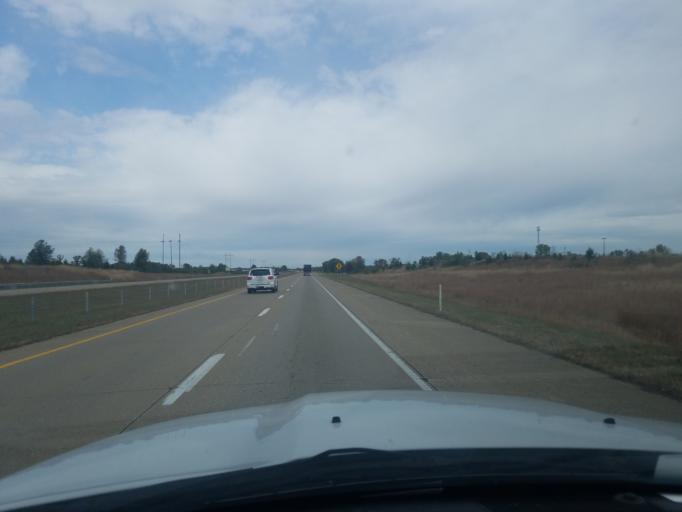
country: US
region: Indiana
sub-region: Vanderburgh County
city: Melody Hill
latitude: 38.0899
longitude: -87.4766
